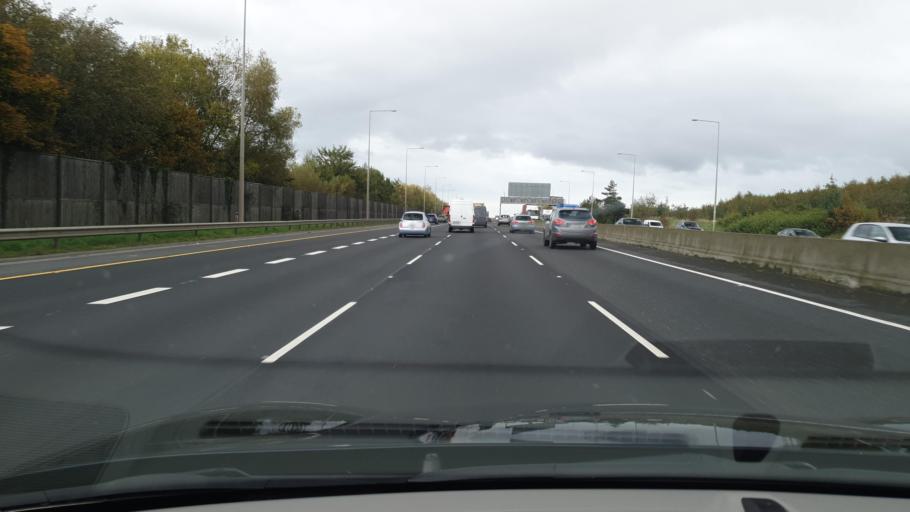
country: IE
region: Leinster
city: Castleknock
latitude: 53.3914
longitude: -6.3437
